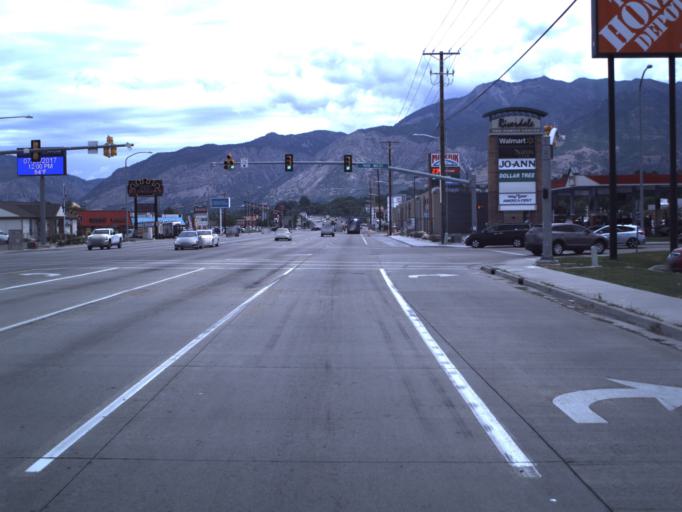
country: US
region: Utah
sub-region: Weber County
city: Riverdale
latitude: 41.1777
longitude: -112.0018
